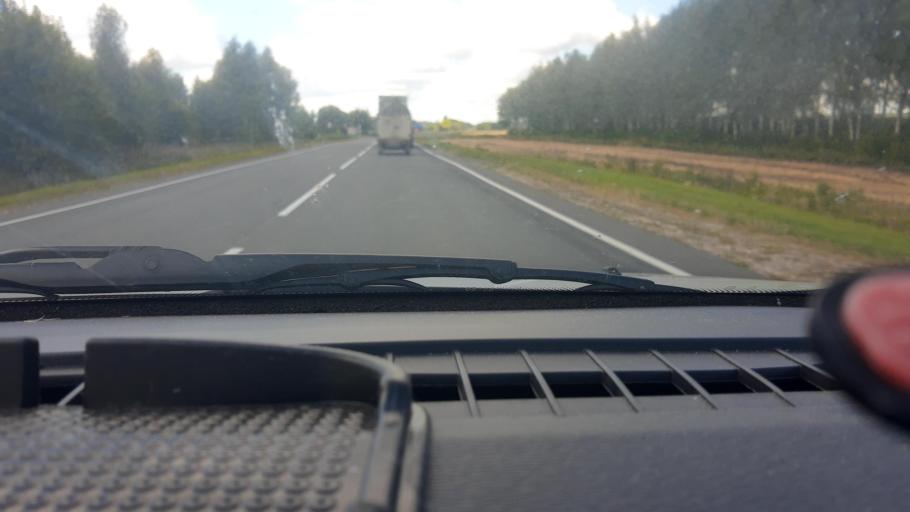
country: RU
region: Nizjnij Novgorod
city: Lukoyanov
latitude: 55.0955
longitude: 44.3064
